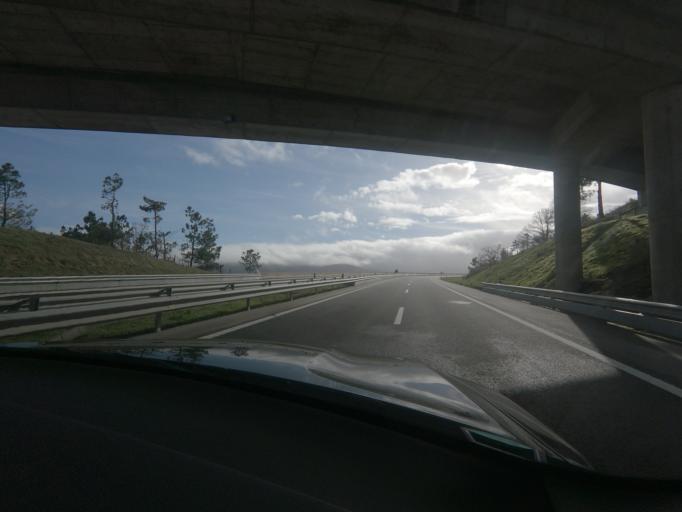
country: PT
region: Viseu
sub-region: Lamego
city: Lamego
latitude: 41.0522
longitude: -7.8408
